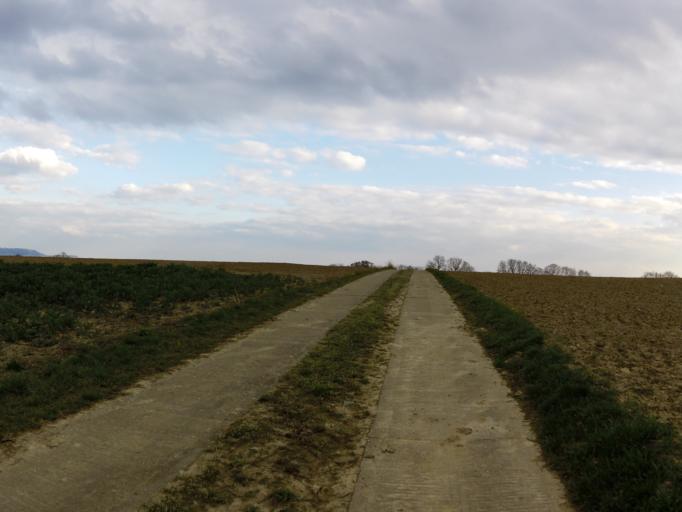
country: DE
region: Bavaria
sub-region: Regierungsbezirk Unterfranken
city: Buchbrunn
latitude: 49.7451
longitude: 10.1149
